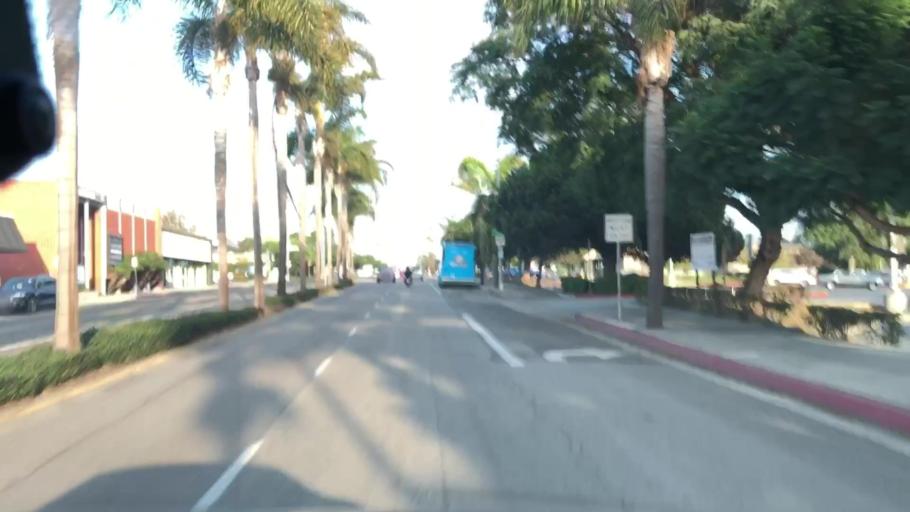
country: US
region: California
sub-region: Ventura County
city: Ventura
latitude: 34.2728
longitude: -119.2494
